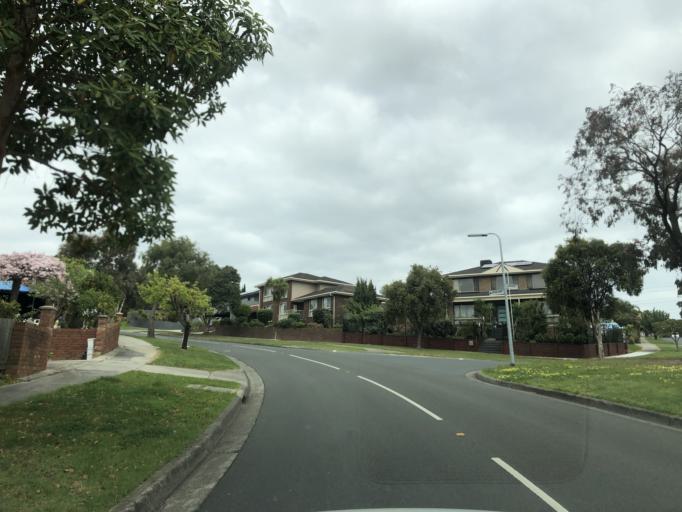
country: AU
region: Victoria
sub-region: Monash
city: Mulgrave
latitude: -37.9282
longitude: 145.1988
